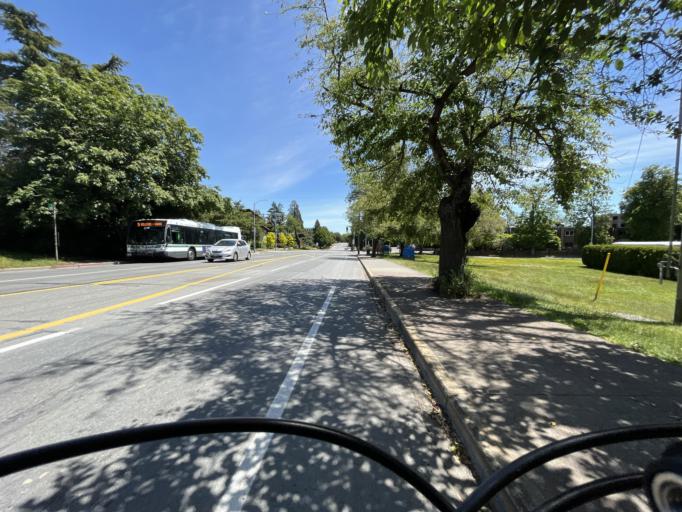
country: CA
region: British Columbia
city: Victoria
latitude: 48.4435
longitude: -123.3871
